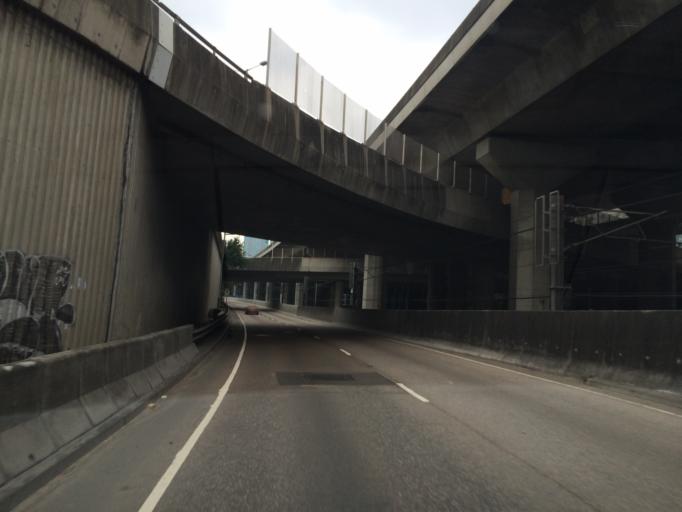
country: HK
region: Sham Shui Po
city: Sham Shui Po
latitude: 22.3271
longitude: 114.1522
